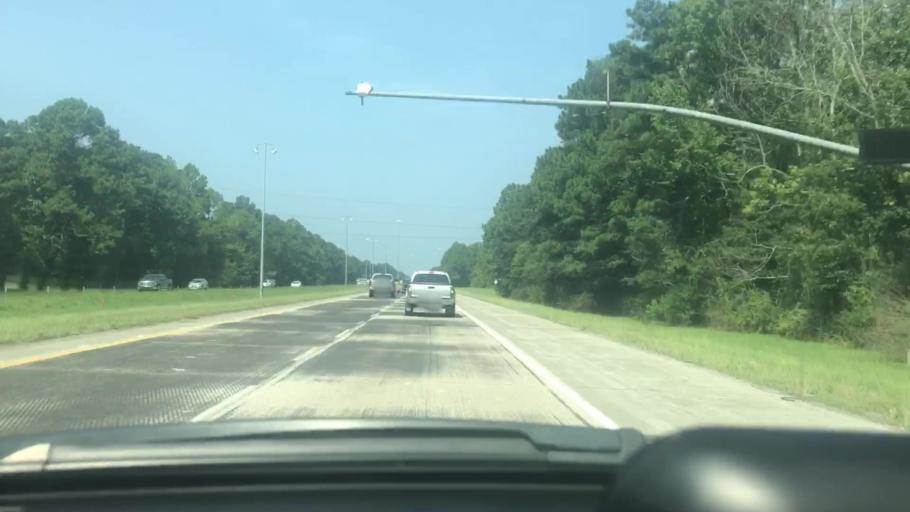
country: US
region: Louisiana
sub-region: Tangipahoa Parish
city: Hammond
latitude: 30.4797
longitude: -90.5124
